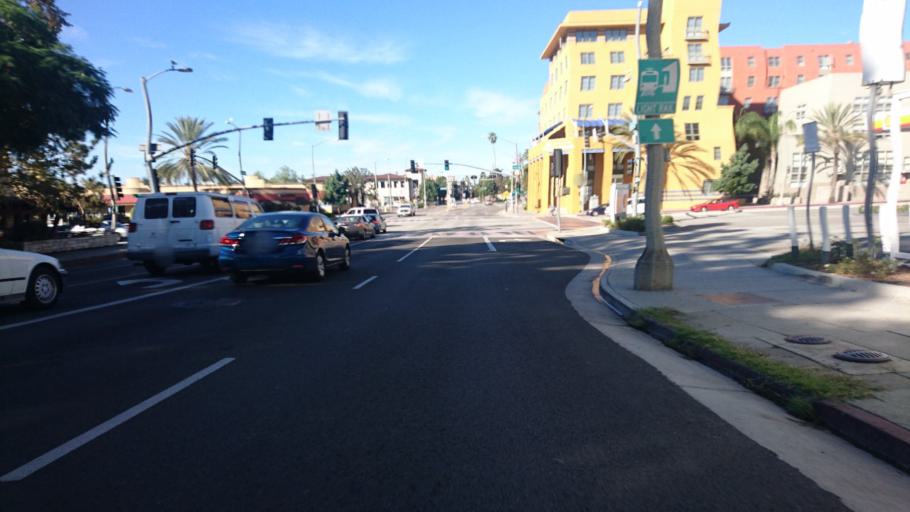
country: US
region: California
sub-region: Los Angeles County
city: Pasadena
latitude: 34.1406
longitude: -118.1468
